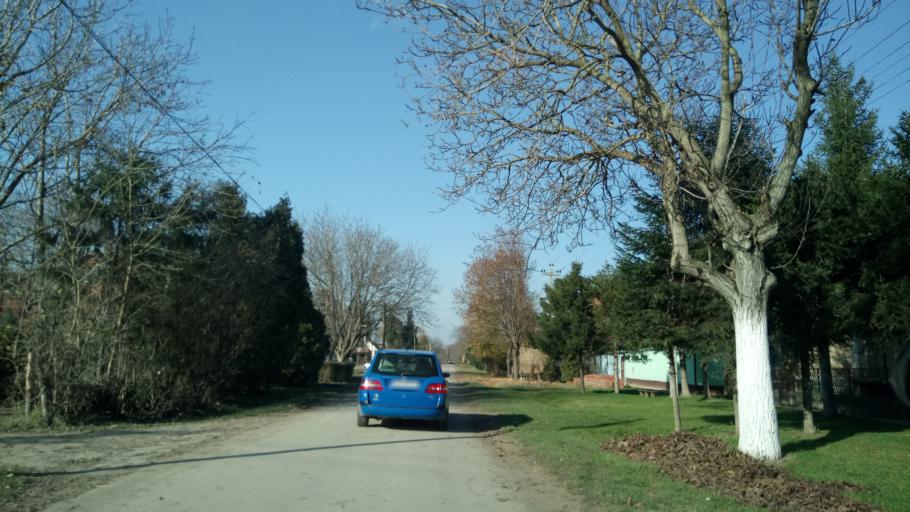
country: RS
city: Ljukovo
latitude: 45.0529
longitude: 20.0264
